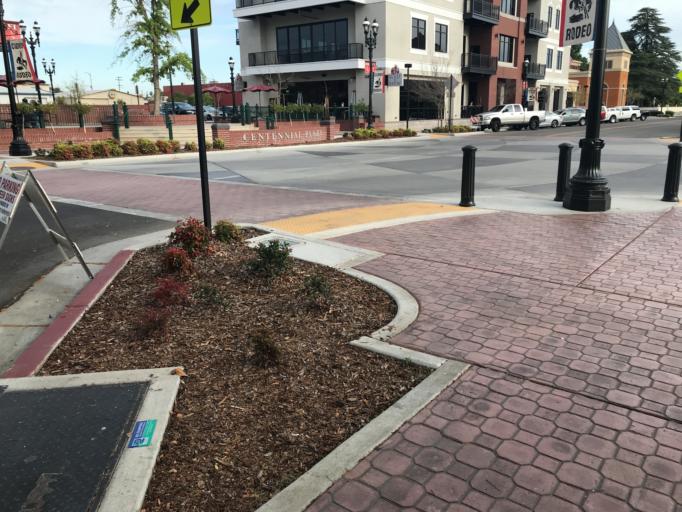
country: US
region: California
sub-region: Fresno County
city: Clovis
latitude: 36.8232
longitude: -119.7022
